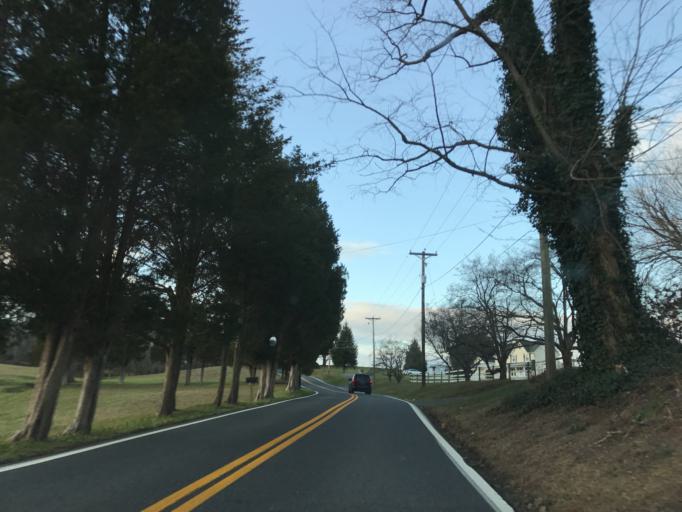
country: US
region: Maryland
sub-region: Cecil County
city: Rising Sun
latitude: 39.6761
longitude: -76.2157
